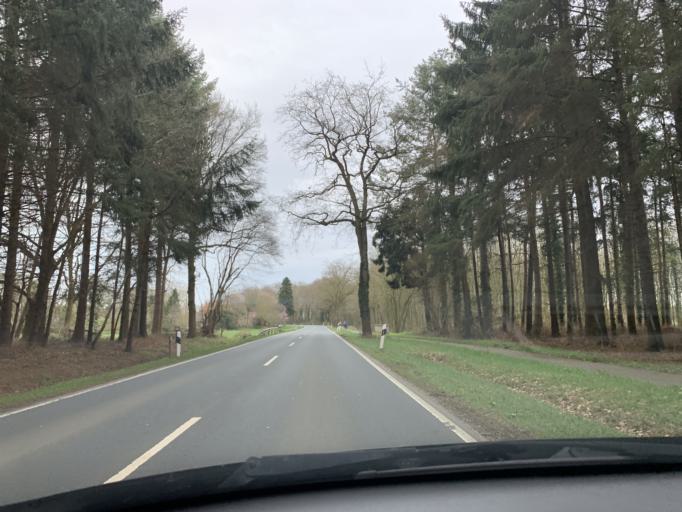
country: DE
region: Lower Saxony
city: Edewecht
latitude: 53.1619
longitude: 7.9627
